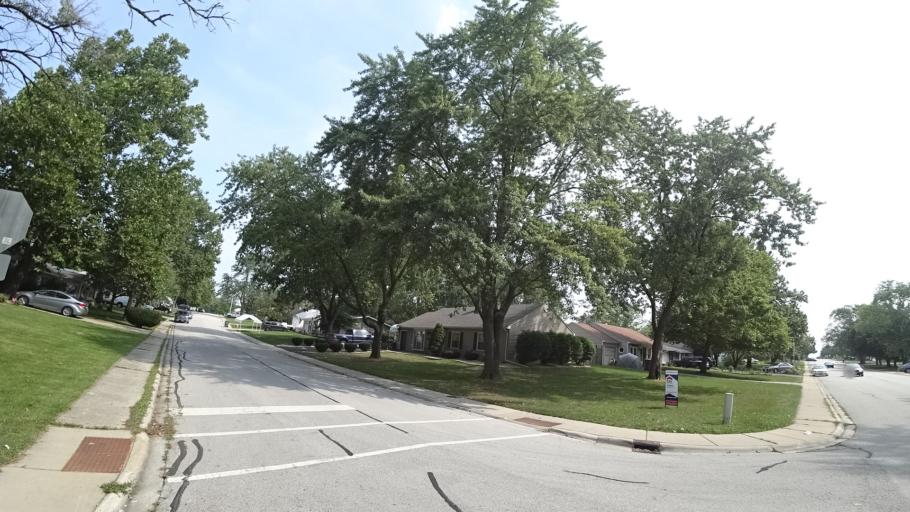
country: US
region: Illinois
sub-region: Cook County
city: Orland Park
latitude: 41.6158
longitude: -87.8656
